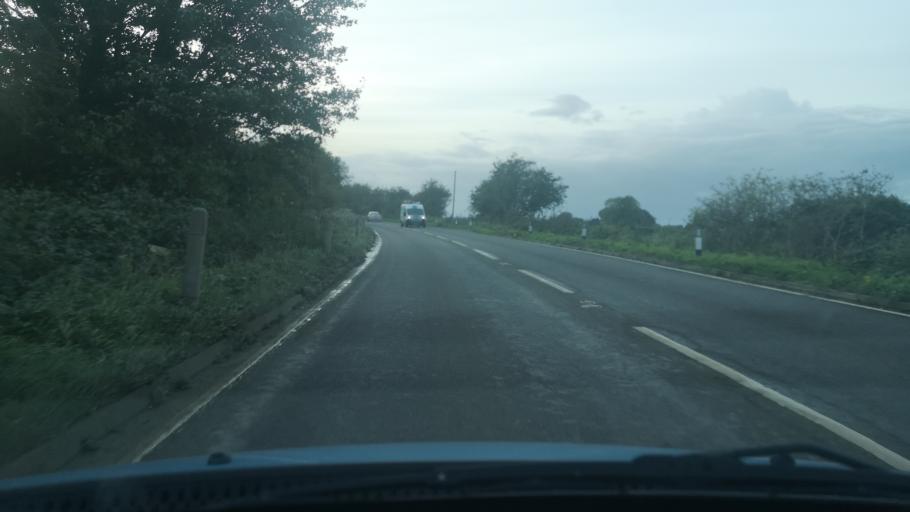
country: GB
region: England
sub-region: North Lincolnshire
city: Crowle
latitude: 53.5877
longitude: -0.8271
